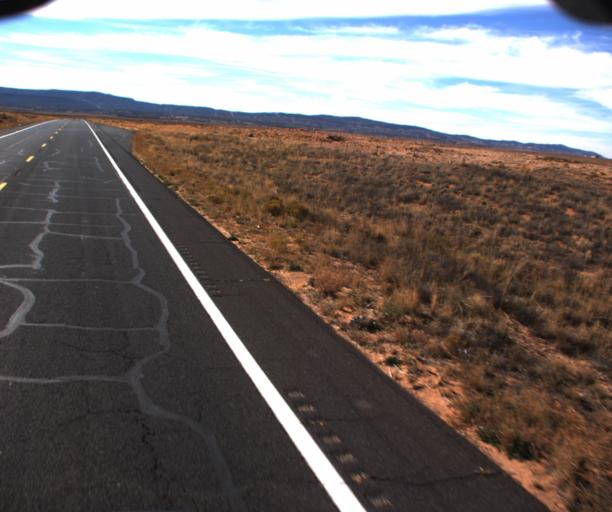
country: US
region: Arizona
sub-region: Coconino County
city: Kaibito
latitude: 36.4889
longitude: -110.7054
